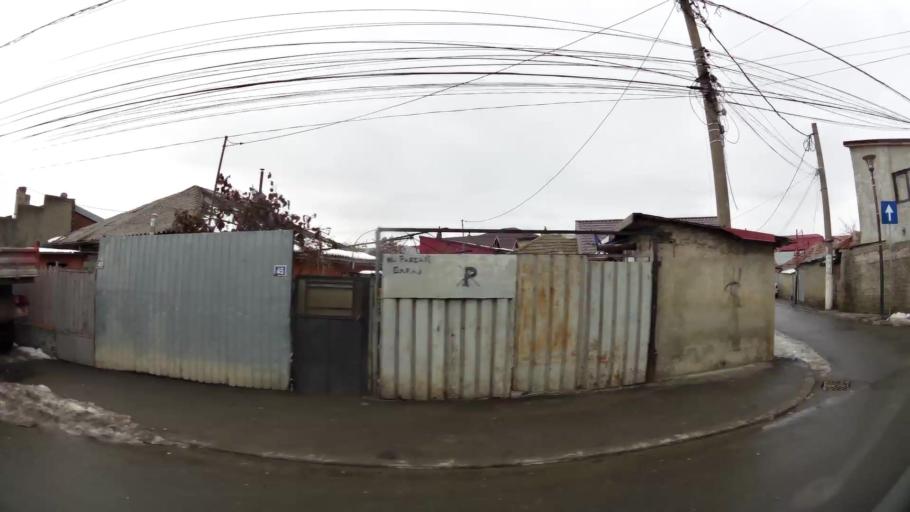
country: RO
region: Ilfov
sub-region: Comuna Pantelimon
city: Pantelimon
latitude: 44.4562
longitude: 26.2003
